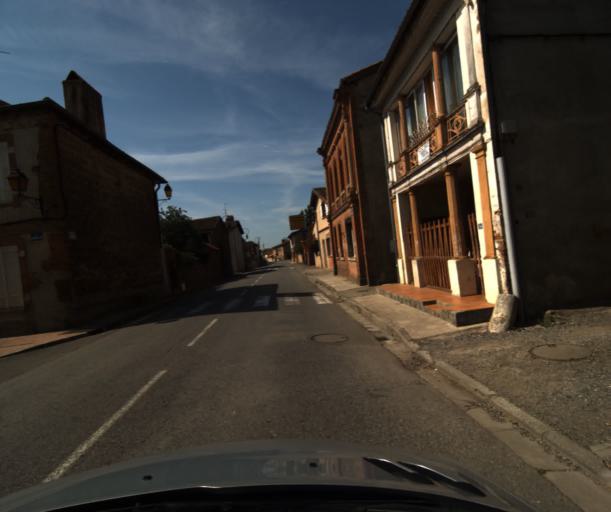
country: FR
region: Midi-Pyrenees
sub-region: Departement de la Haute-Garonne
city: Labastidette
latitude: 43.4654
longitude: 1.2159
